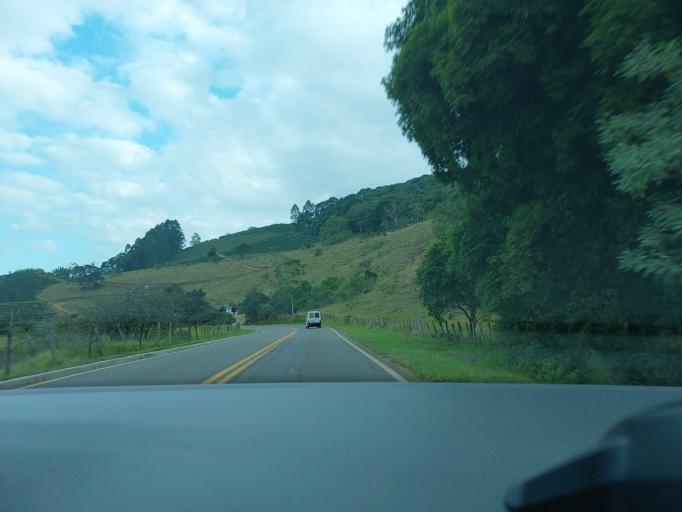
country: BR
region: Minas Gerais
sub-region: Mirai
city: Mirai
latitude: -21.0183
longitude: -42.5427
